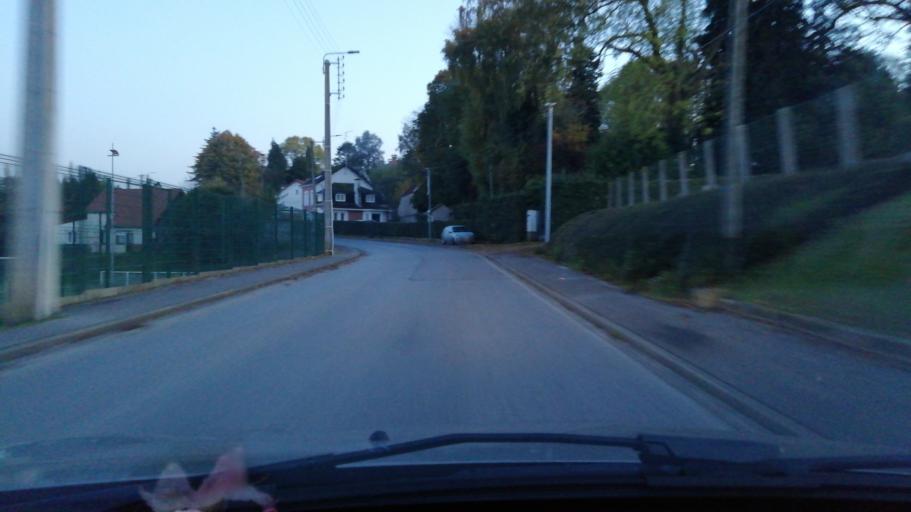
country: FR
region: Nord-Pas-de-Calais
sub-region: Departement du Nord
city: Marpent
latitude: 50.2876
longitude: 4.0853
